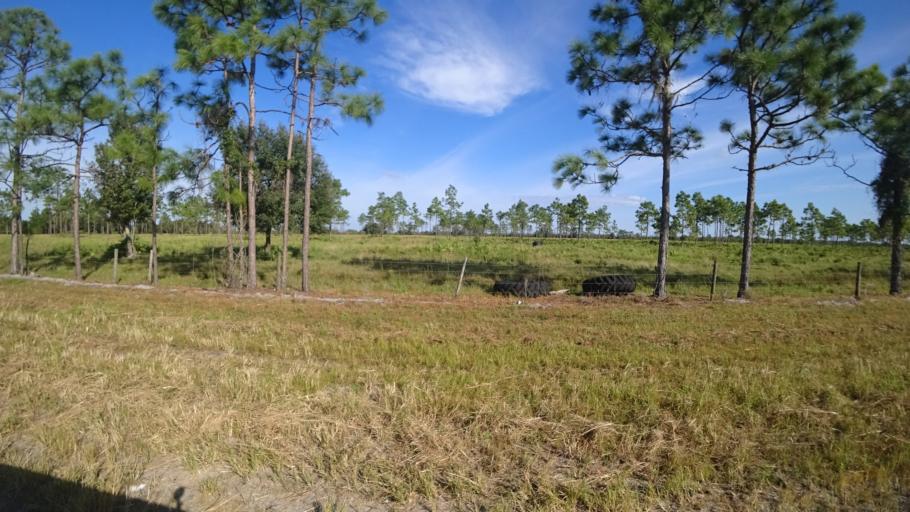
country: US
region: Florida
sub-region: Sarasota County
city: The Meadows
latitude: 27.4449
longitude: -82.3346
